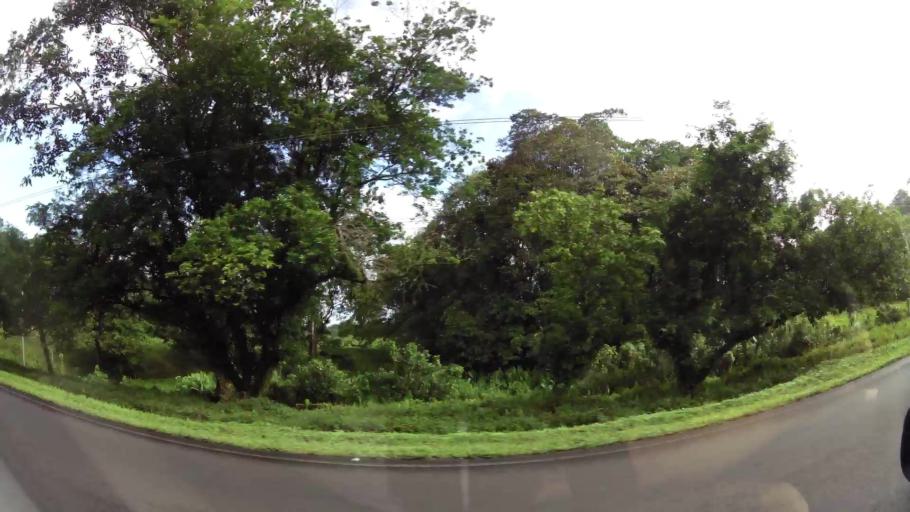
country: CR
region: Limon
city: Pocora
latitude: 10.1863
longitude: -83.6318
